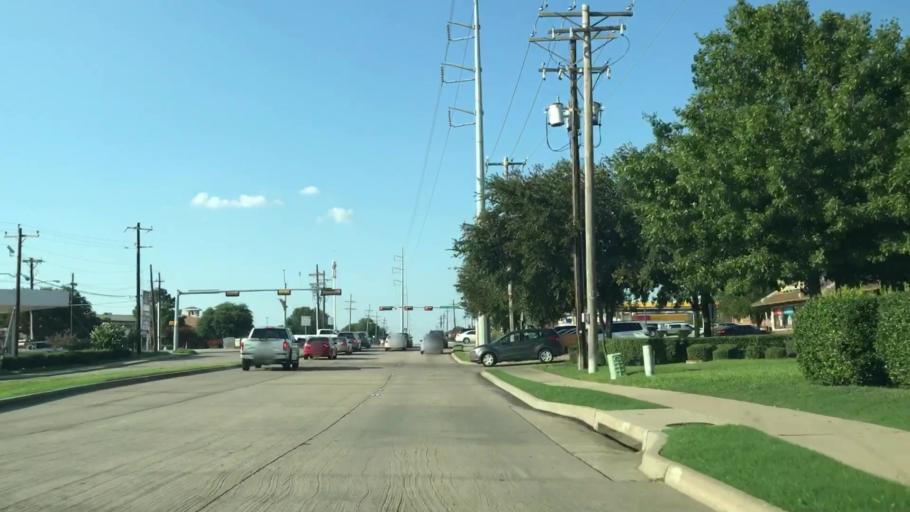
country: US
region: Texas
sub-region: Denton County
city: Lewisville
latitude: 33.0414
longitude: -97.0360
